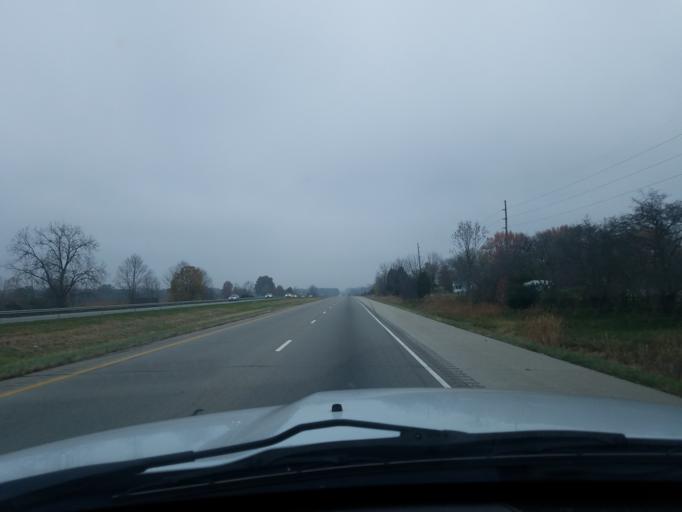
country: US
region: Indiana
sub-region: Bartholomew County
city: Columbus
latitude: 39.1545
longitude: -85.9581
